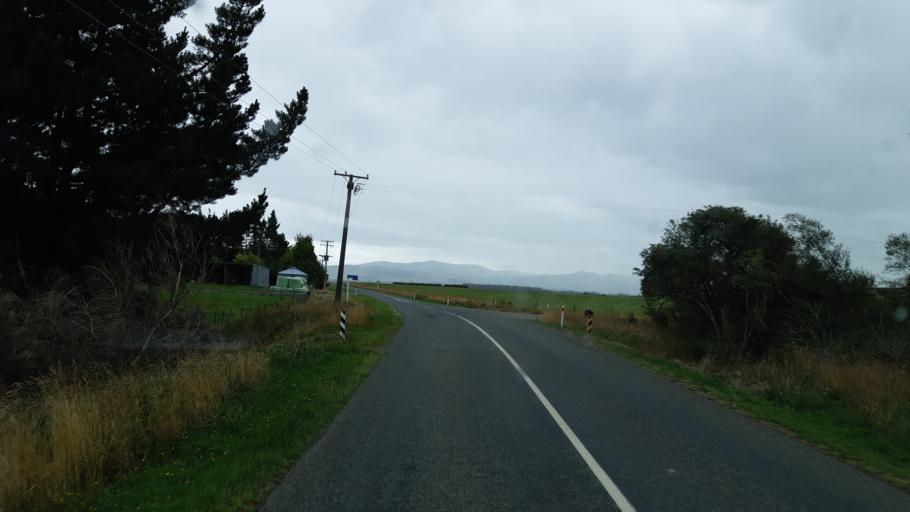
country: NZ
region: Southland
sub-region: Southland District
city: Winton
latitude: -45.7626
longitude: 168.4951
